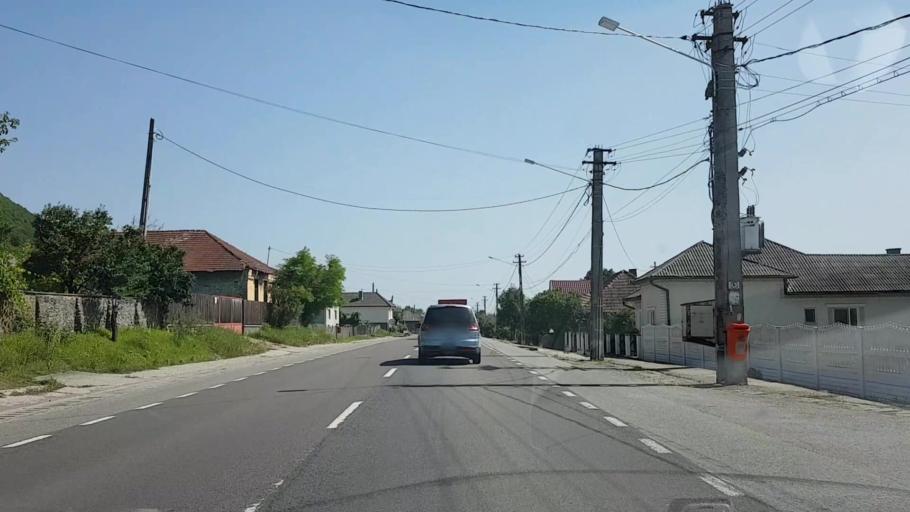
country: RO
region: Bistrita-Nasaud
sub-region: Comuna Sieu-Odorhei
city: Sieu-Odorhei
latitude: 47.1443
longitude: 24.3066
